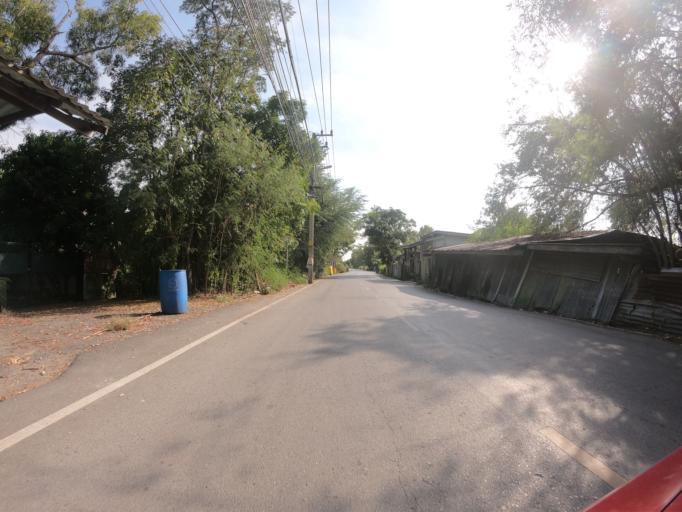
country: TH
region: Pathum Thani
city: Thanyaburi
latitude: 14.0098
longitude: 100.7318
